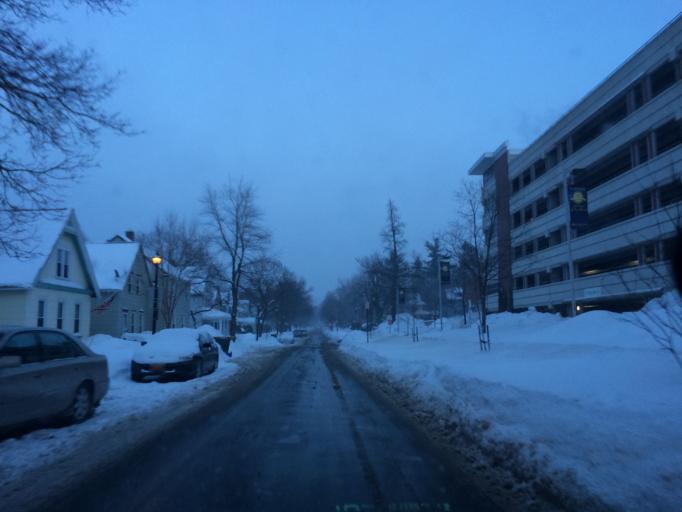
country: US
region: New York
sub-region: Monroe County
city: Rochester
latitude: 43.1367
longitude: -77.6064
